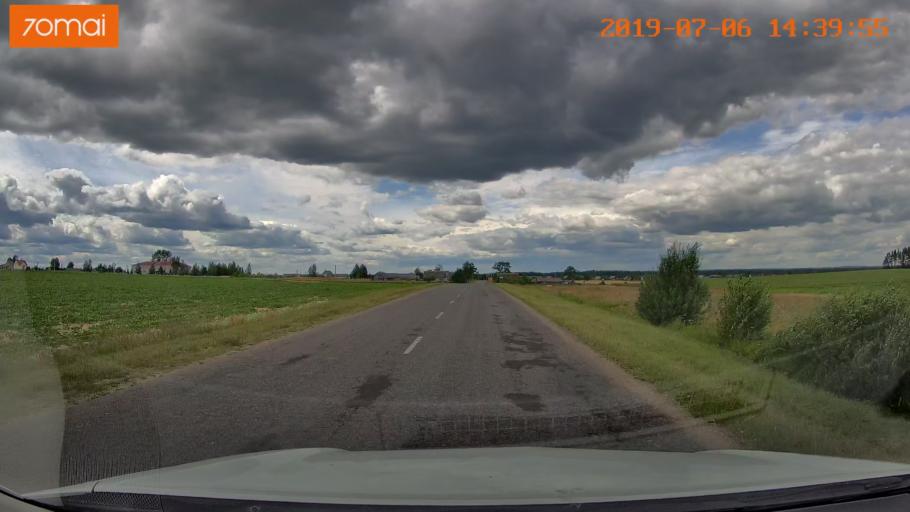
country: BY
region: Minsk
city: Ivyanyets
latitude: 53.9207
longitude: 26.6806
